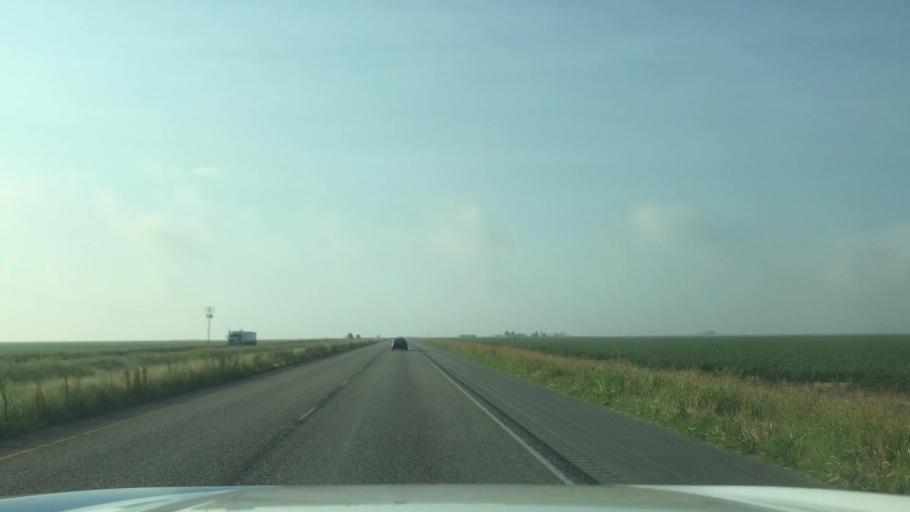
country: US
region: Texas
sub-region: Lubbock County
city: Slaton
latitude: 33.3252
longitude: -101.5297
